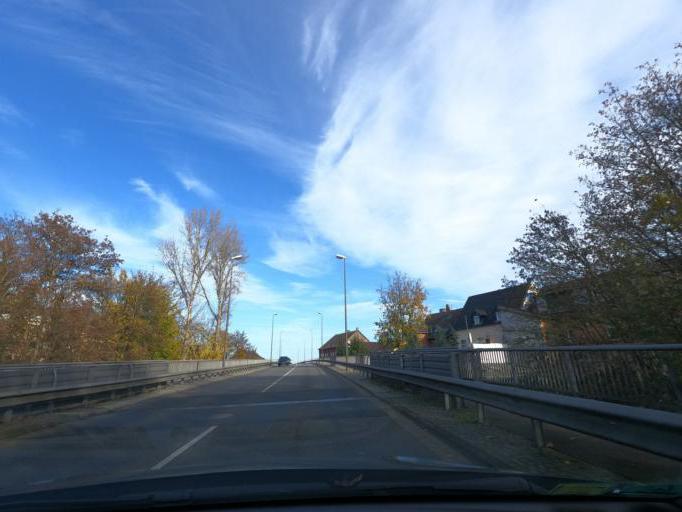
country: DE
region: Lower Saxony
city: Peine
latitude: 52.3163
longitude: 10.2336
